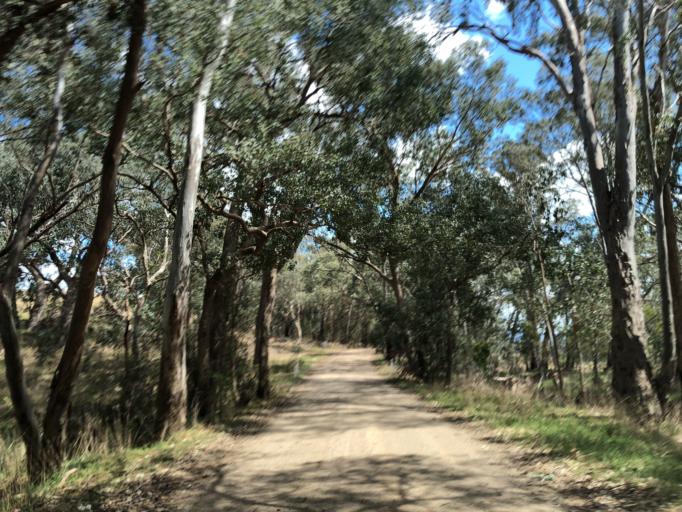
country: AU
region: Victoria
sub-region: Benalla
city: Benalla
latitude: -36.7297
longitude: 146.1267
